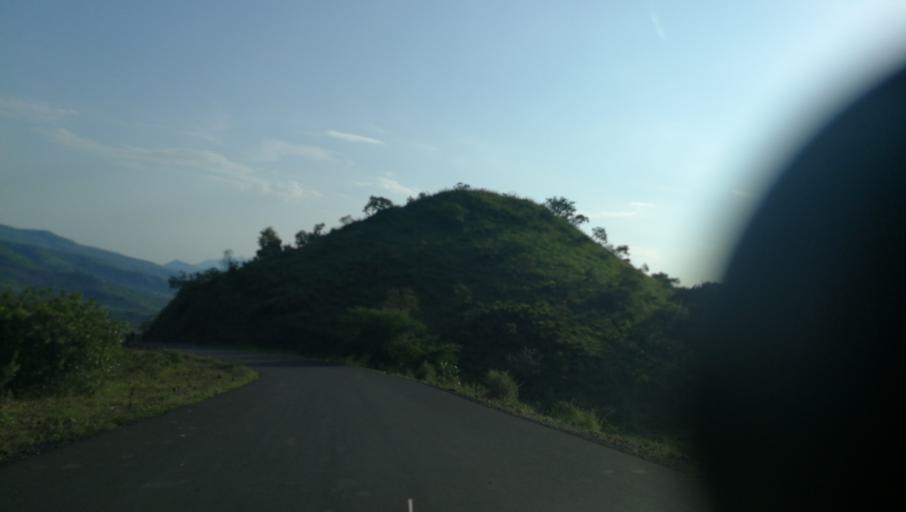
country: ET
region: Southern Nations, Nationalities, and People's Region
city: Areka
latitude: 6.8283
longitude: 37.3081
